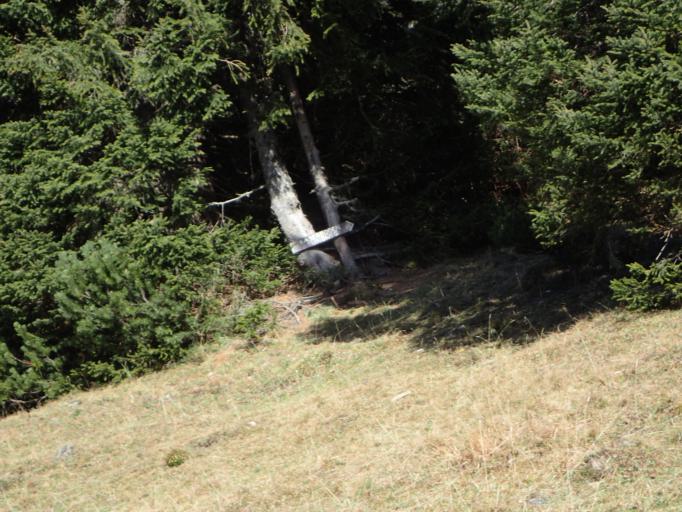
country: AT
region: Salzburg
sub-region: Politischer Bezirk Zell am See
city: Dienten am Hochkonig
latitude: 47.4068
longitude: 13.0227
